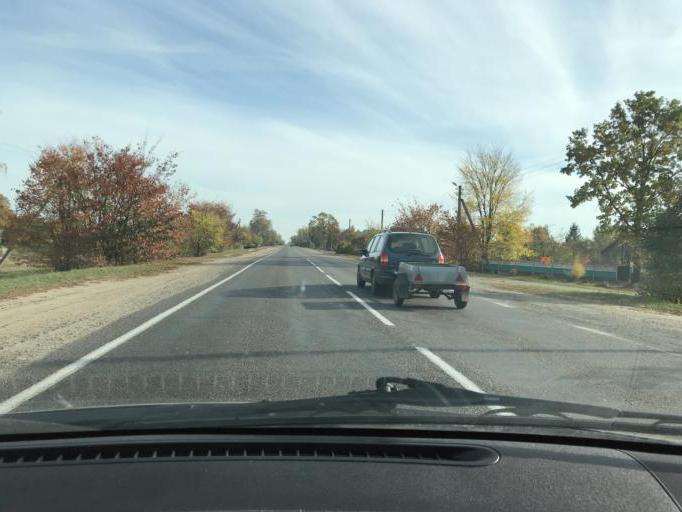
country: BY
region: Brest
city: Lahishyn
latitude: 52.2344
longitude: 26.0125
